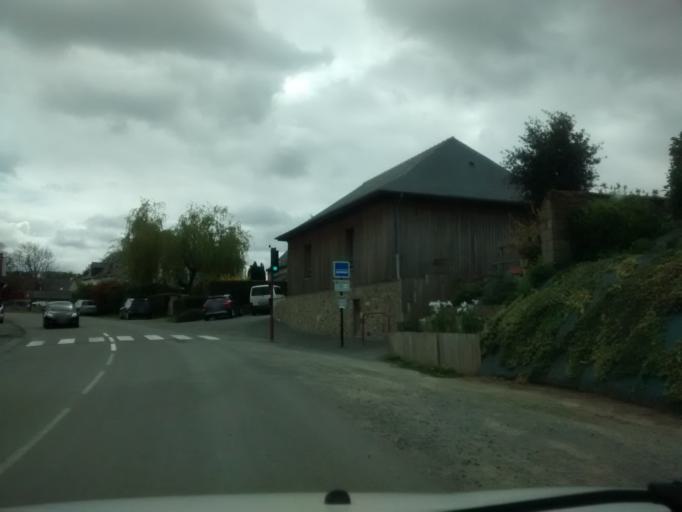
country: FR
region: Brittany
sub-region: Departement d'Ille-et-Vilaine
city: Saint-Jouan-des-Guerets
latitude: 48.5718
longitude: -1.9693
